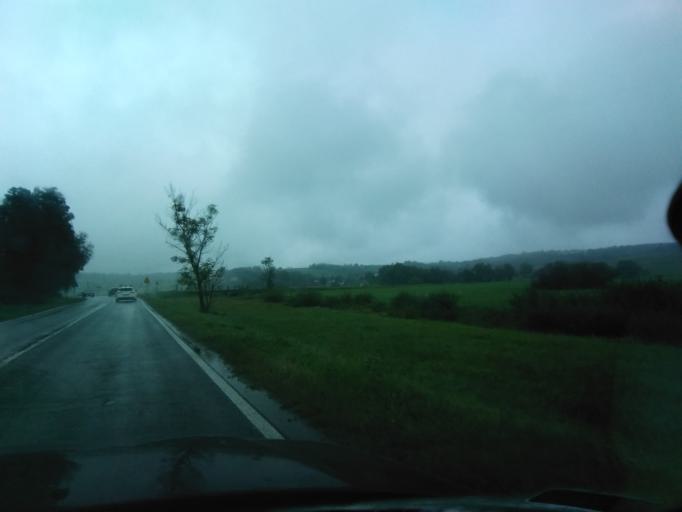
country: PL
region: Subcarpathian Voivodeship
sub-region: Powiat ropczycko-sedziszowski
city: Niedzwiada
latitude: 49.9768
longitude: 21.5626
